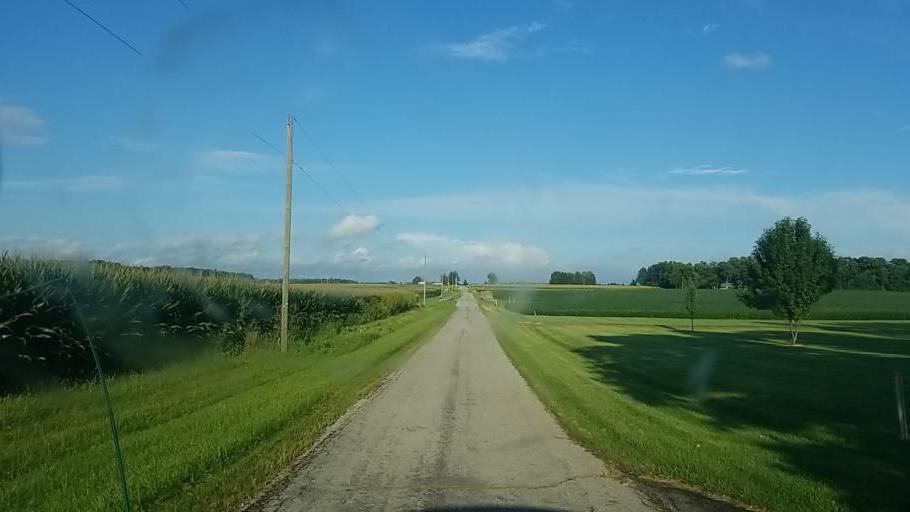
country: US
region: Ohio
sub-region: Crawford County
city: Bucyrus
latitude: 40.7396
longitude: -82.9598
